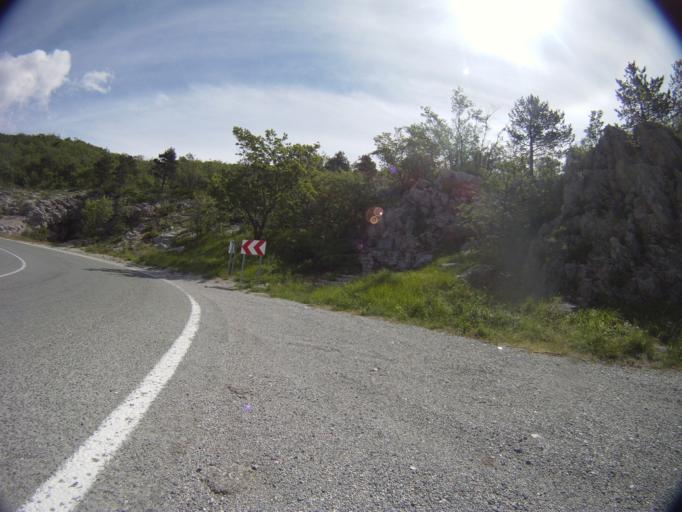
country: HR
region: Primorsko-Goranska
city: Cernik
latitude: 45.3775
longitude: 14.5421
